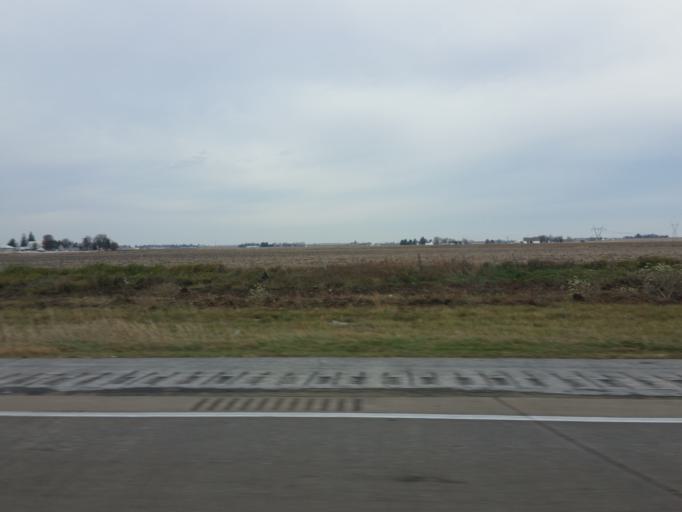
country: US
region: Iowa
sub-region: Scott County
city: Walcott
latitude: 41.6038
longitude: -90.6965
